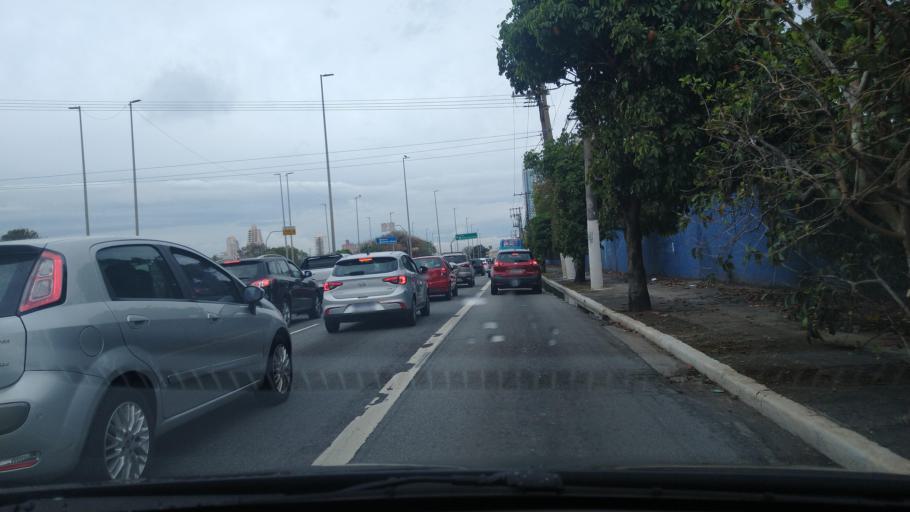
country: SA
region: Ar Riyad
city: Ad Dilam
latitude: 23.5153
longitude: 46.6734
